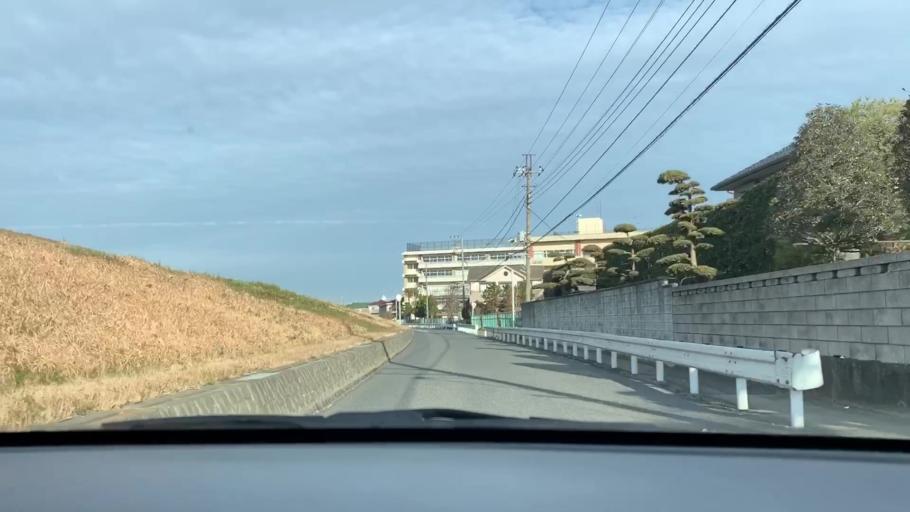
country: JP
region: Chiba
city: Matsudo
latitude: 35.8033
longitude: 139.8941
